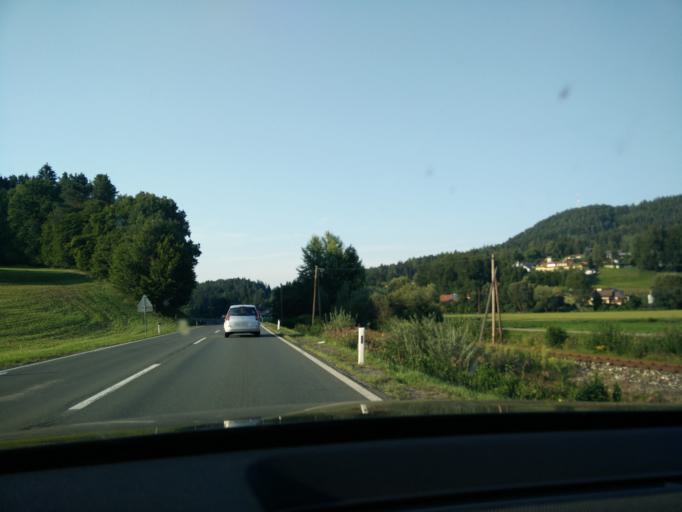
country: AT
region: Carinthia
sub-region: Politischer Bezirk Klagenfurt Land
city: Maria Rain
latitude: 46.5683
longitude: 14.2854
